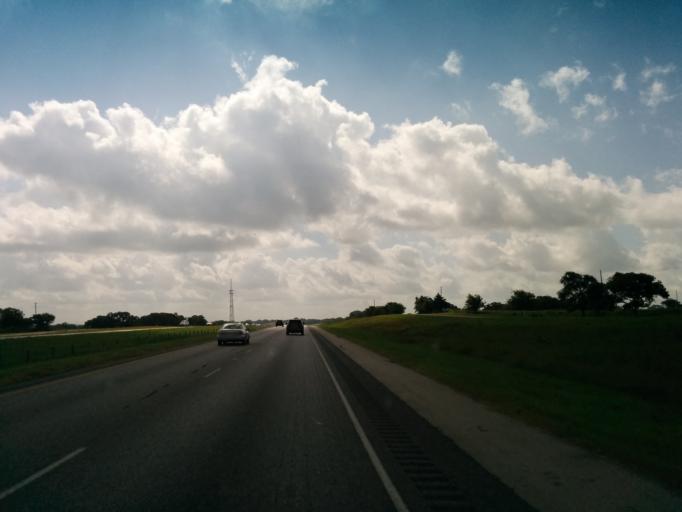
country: US
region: Texas
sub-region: Fayette County
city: Flatonia
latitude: 29.6936
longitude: -97.0203
